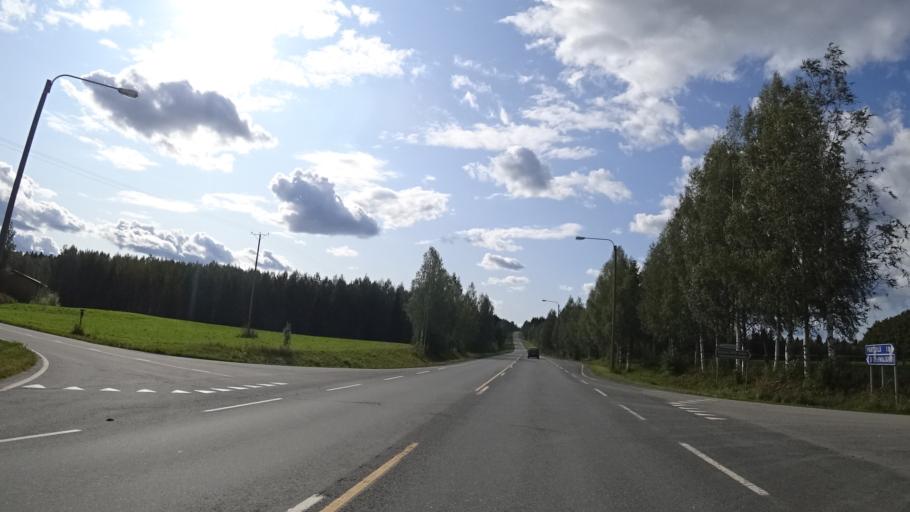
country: FI
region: North Karelia
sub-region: Keski-Karjala
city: Tohmajaervi
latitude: 62.2214
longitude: 30.3823
